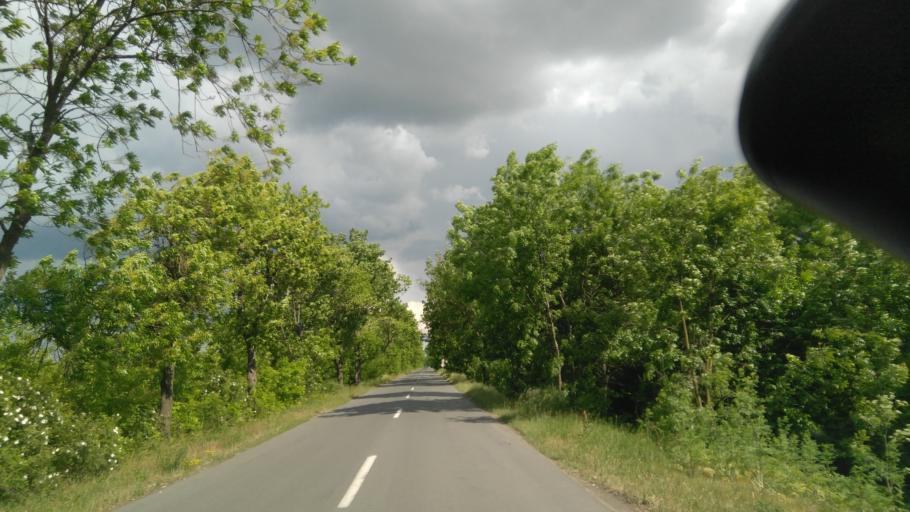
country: HU
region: Bekes
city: Bucsa
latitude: 47.1973
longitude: 21.0116
